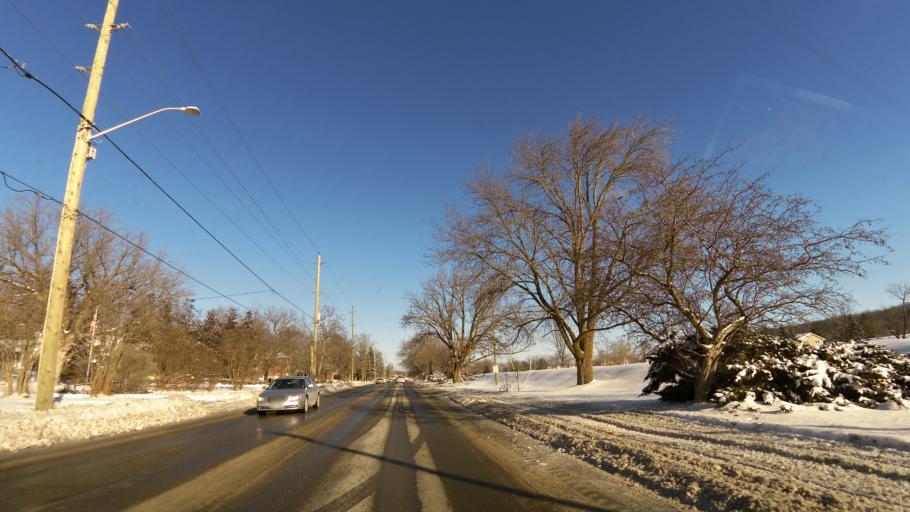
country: CA
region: Ontario
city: Quinte West
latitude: 44.2973
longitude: -77.8057
